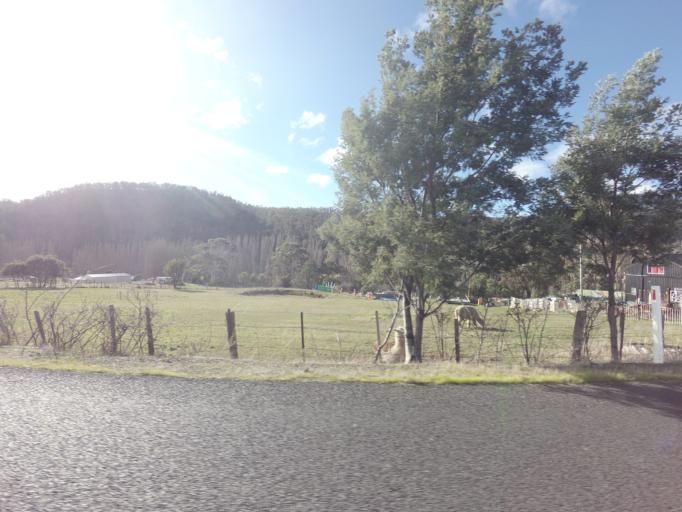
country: AU
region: Tasmania
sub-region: Derwent Valley
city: New Norfolk
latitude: -42.7999
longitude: 147.1366
